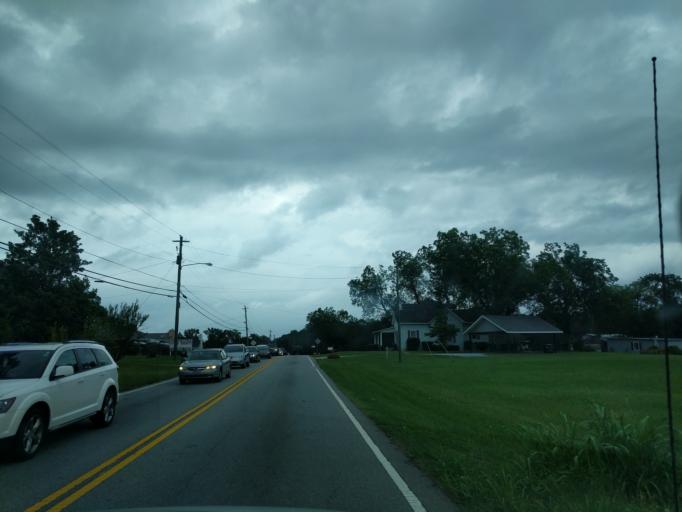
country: US
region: Georgia
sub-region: Walton County
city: Loganville
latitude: 33.8452
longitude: -83.8973
